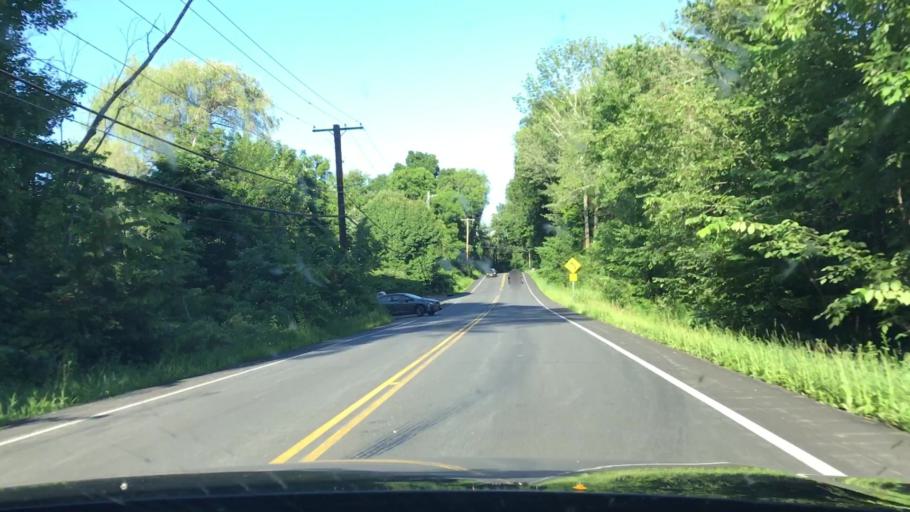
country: US
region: New York
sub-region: Putnam County
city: Mahopac
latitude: 41.3765
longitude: -73.7168
